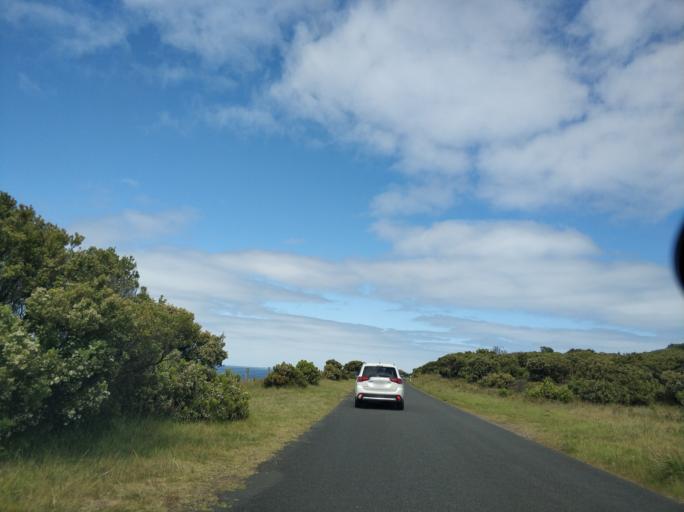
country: AU
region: Victoria
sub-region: Colac-Otway
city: Apollo Bay
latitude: -38.8499
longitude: 143.5355
